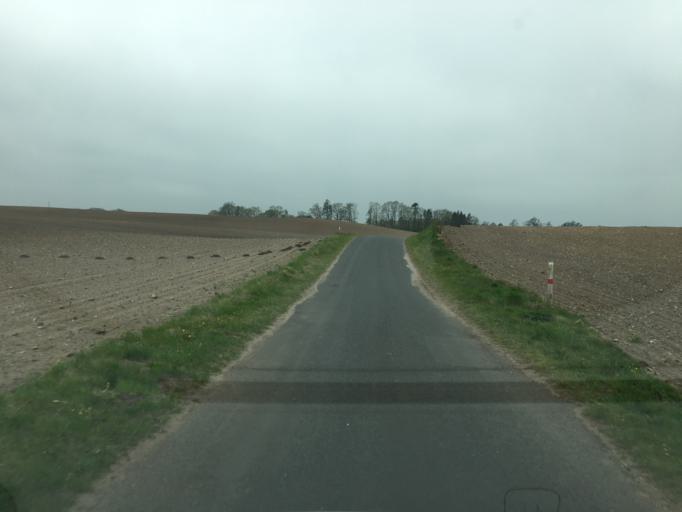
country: DK
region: South Denmark
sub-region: Aabenraa Kommune
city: Krusa
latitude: 54.8887
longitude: 9.4092
